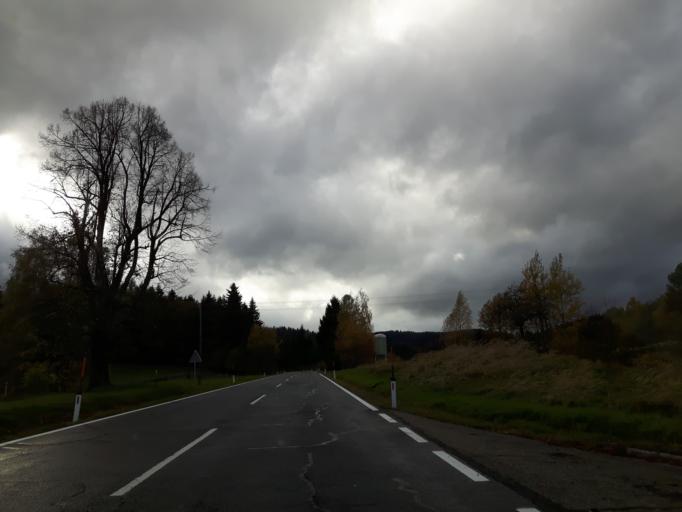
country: AT
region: Styria
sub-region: Politischer Bezirk Deutschlandsberg
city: Sankt Oswald ob Eibiswald
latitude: 46.7018
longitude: 15.1286
